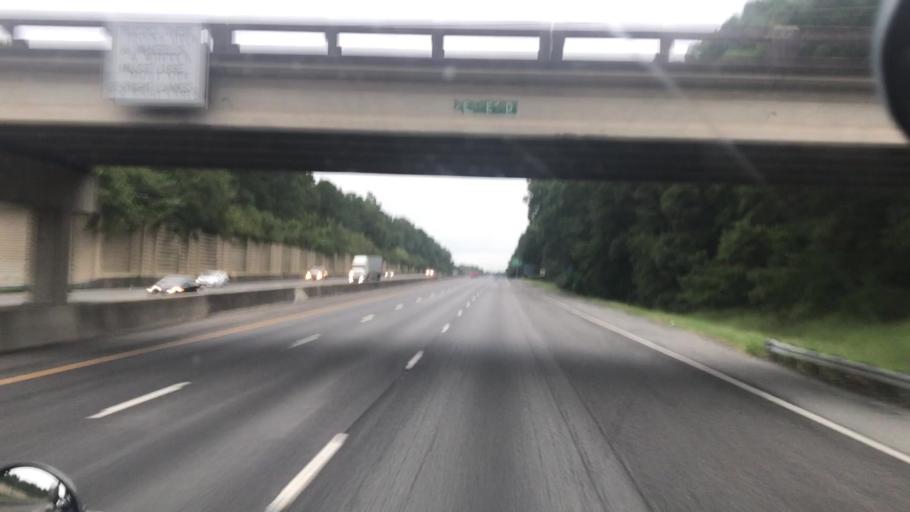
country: US
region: Georgia
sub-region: Bibb County
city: West Point
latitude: 32.8699
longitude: -83.7577
